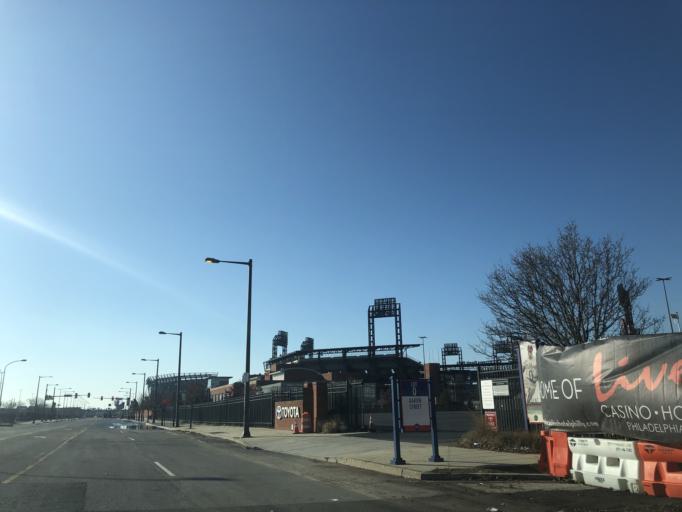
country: US
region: Pennsylvania
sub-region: Philadelphia County
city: Philadelphia
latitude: 39.9083
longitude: -75.1637
